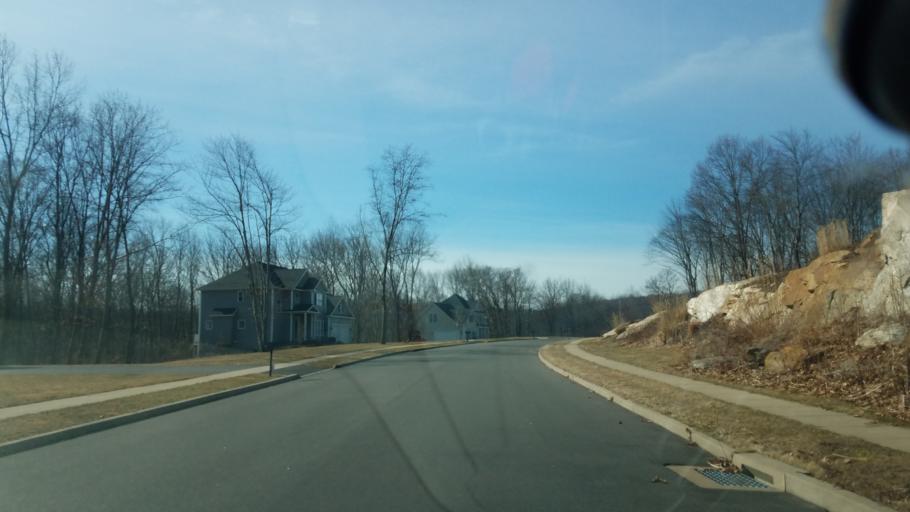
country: US
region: Connecticut
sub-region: New Haven County
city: Prospect
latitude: 41.5348
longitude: -72.9618
